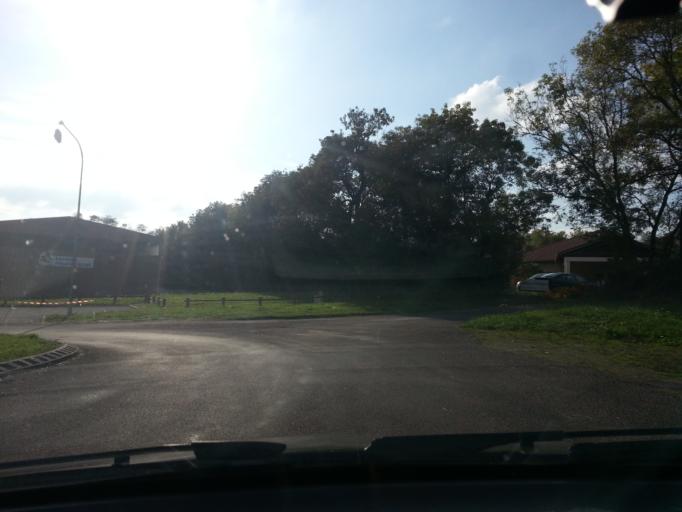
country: FR
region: Bourgogne
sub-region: Departement de Saone-et-Loire
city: Chatenoy-le-Royal
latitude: 46.7942
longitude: 4.7881
